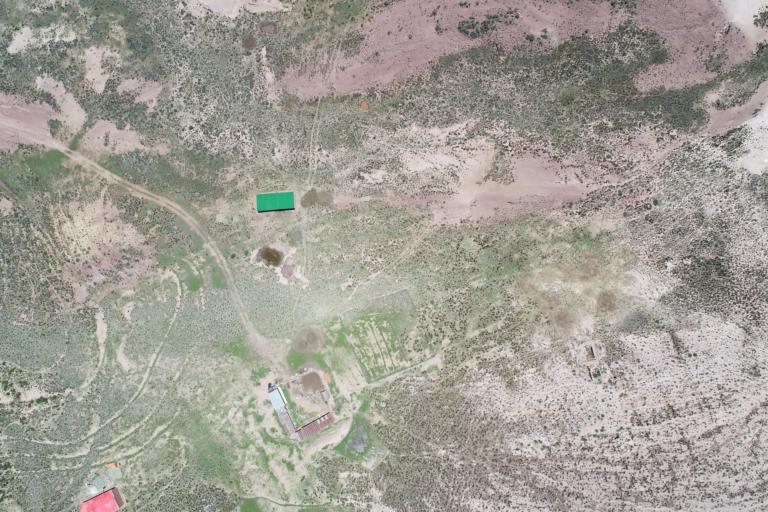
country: BO
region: La Paz
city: Patacamaya
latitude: -17.2749
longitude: -68.5028
